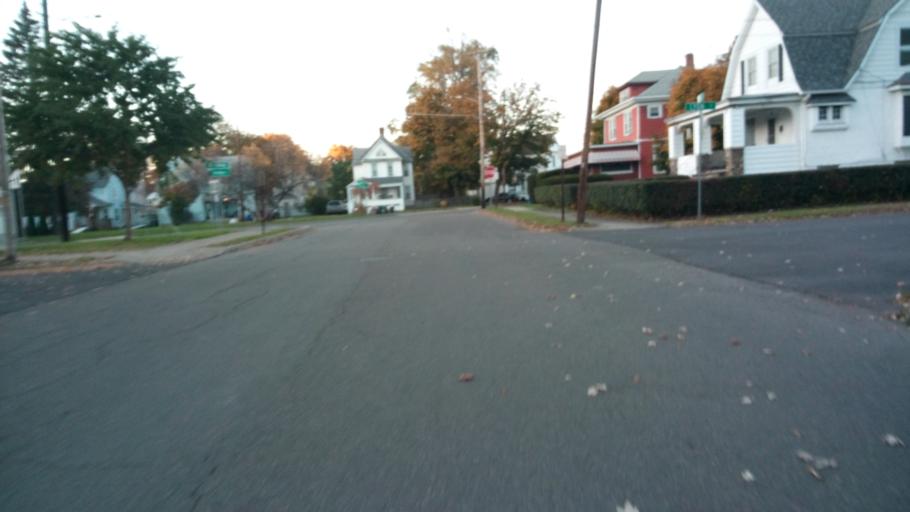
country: US
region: New York
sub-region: Chemung County
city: Southport
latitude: 42.0704
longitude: -76.8138
